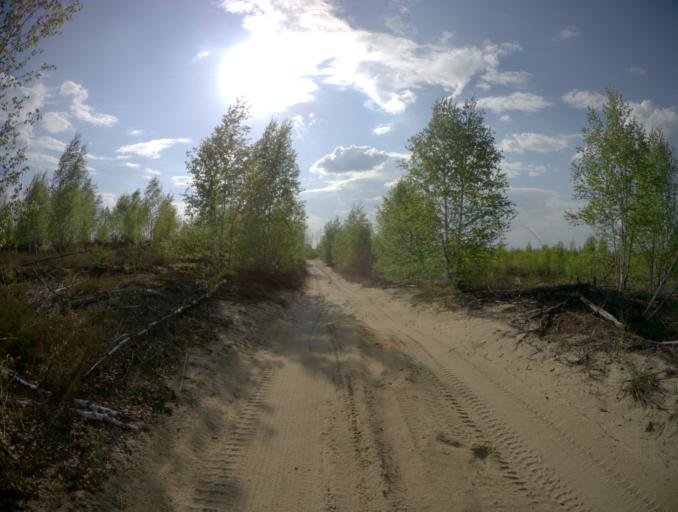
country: RU
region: Ivanovo
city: Talitsy
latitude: 56.4150
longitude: 42.2599
